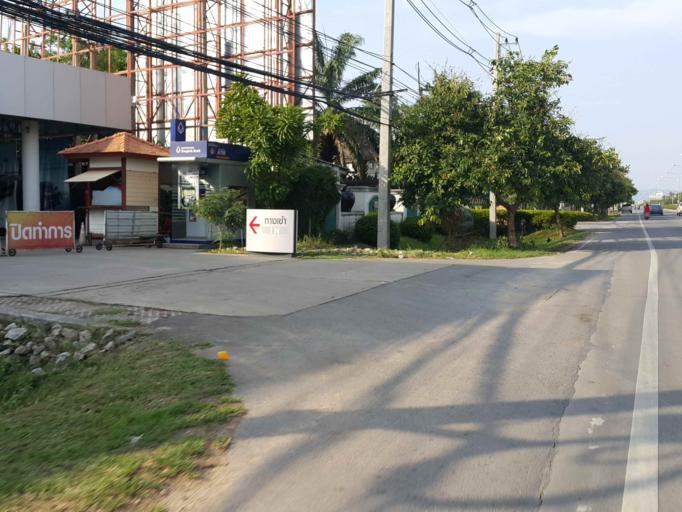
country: TH
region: Chiang Mai
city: San Sai
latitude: 18.8162
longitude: 99.0350
